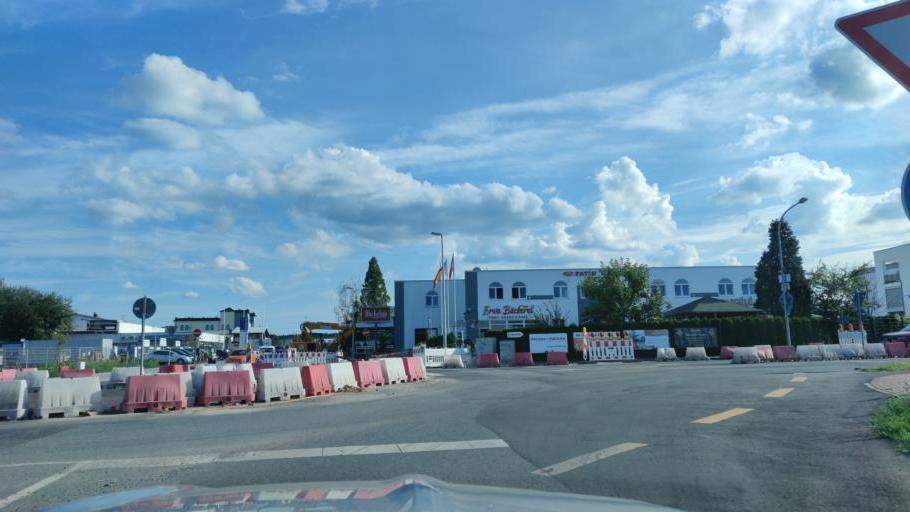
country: DE
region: Hesse
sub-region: Regierungsbezirk Darmstadt
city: Dietzenbach
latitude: 50.0091
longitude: 8.7920
